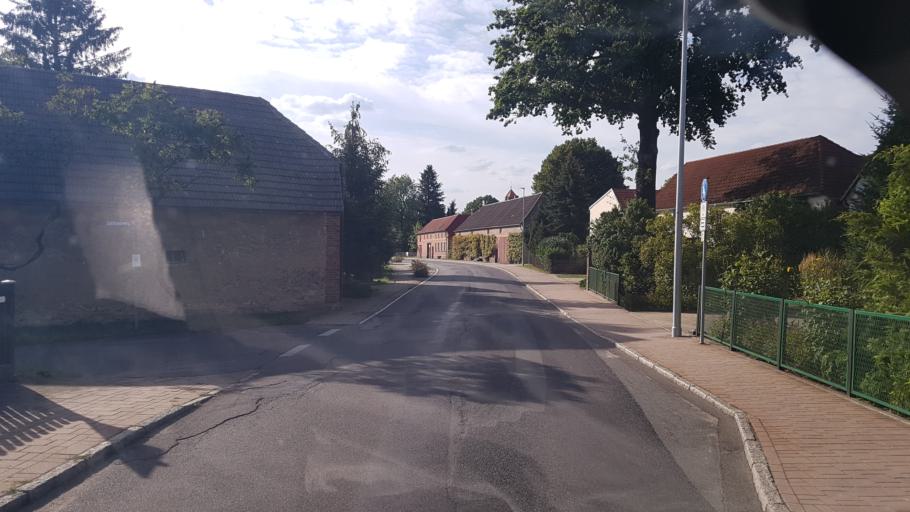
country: DE
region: Brandenburg
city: Welzow
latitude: 51.5514
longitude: 14.1924
